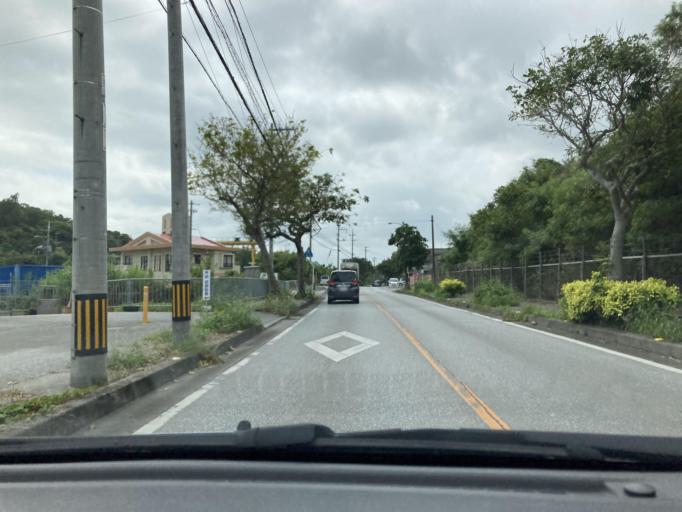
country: JP
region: Okinawa
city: Ginowan
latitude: 26.2783
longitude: 127.7834
